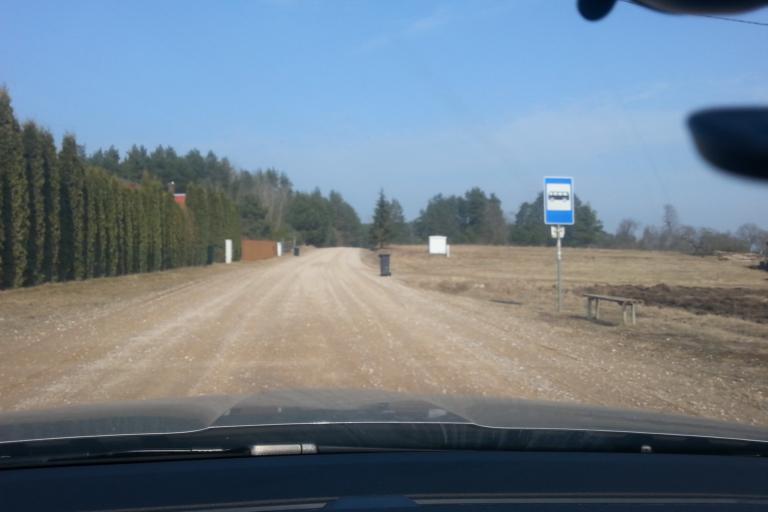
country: LT
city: Trakai
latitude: 54.5707
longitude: 24.9677
